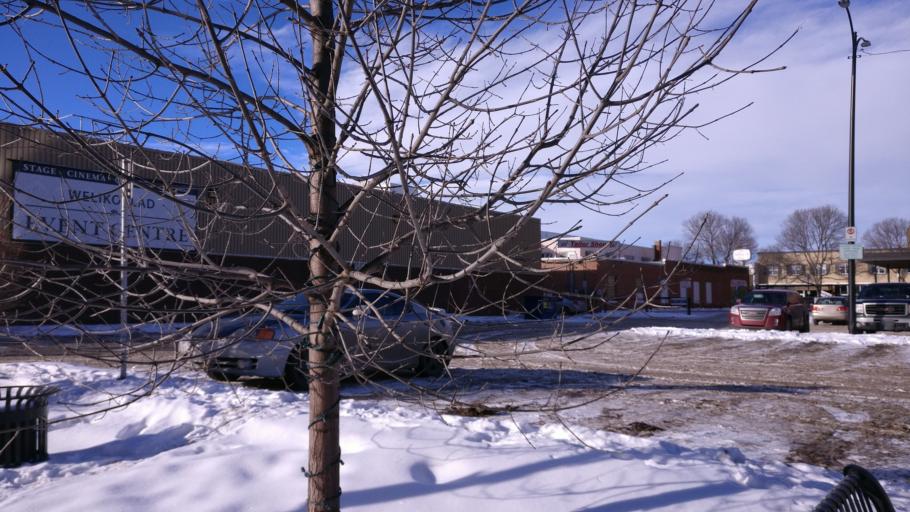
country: CA
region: Alberta
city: Red Deer
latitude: 52.2681
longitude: -113.8125
